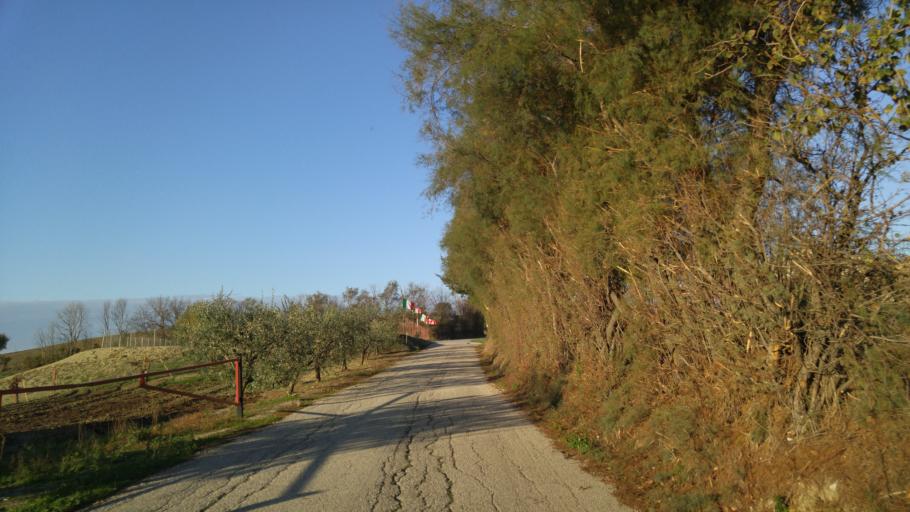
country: IT
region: The Marches
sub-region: Provincia di Pesaro e Urbino
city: Cartoceto
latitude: 43.7909
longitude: 12.8990
